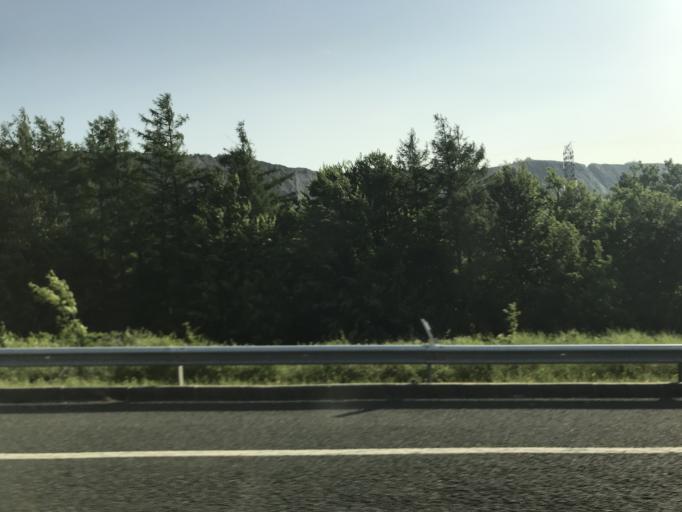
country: ES
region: Navarre
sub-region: Provincia de Navarra
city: Altsasu
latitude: 42.9204
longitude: -2.2054
